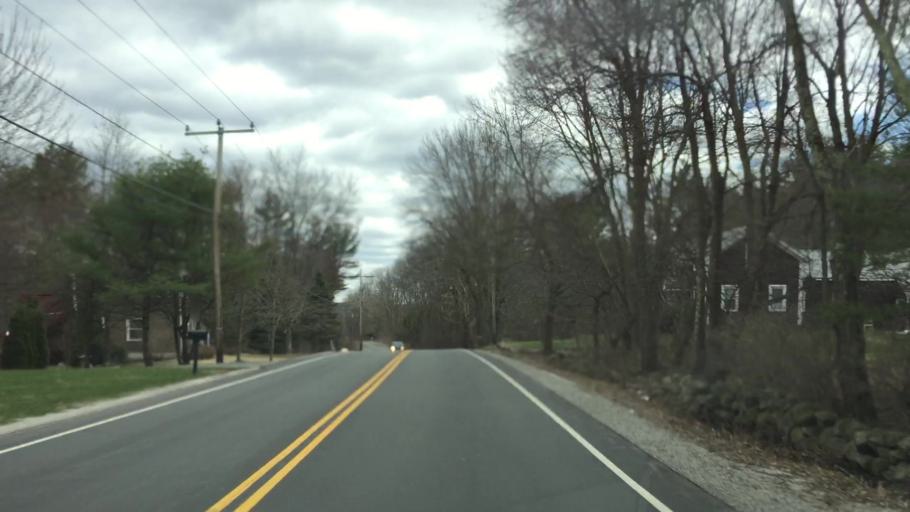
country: US
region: New Hampshire
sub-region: Rockingham County
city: Londonderry
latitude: 42.8140
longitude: -71.3590
